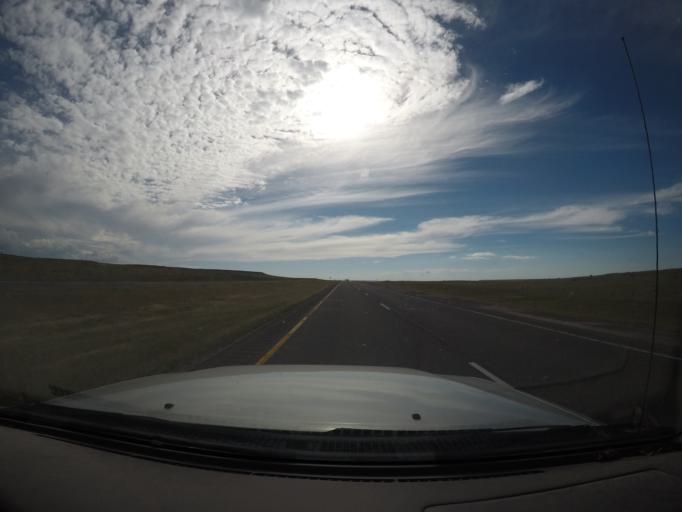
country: US
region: Wyoming
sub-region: Laramie County
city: Pine Bluffs
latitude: 41.1925
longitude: -103.9730
